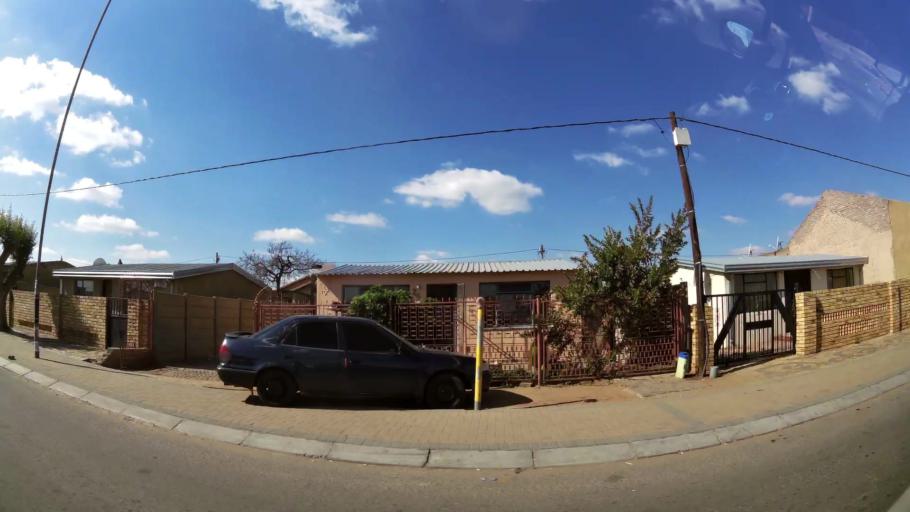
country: ZA
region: Gauteng
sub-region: West Rand District Municipality
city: Krugersdorp
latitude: -26.1569
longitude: 27.7841
